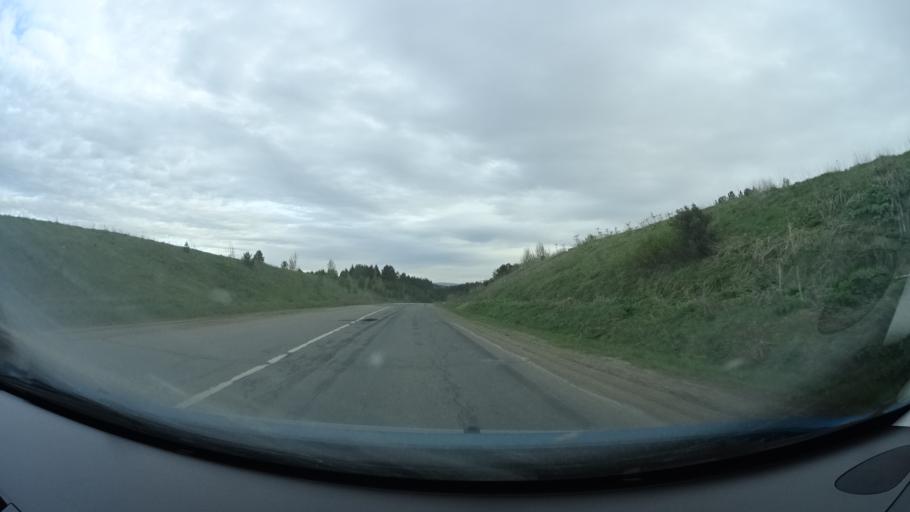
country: RU
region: Perm
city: Osa
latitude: 57.2624
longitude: 55.5752
